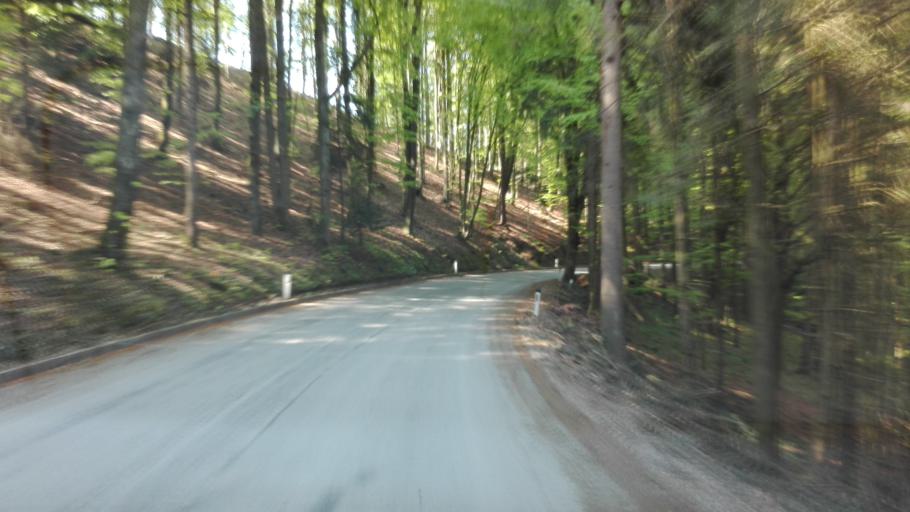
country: AT
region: Upper Austria
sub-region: Politischer Bezirk Rohrbach
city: Atzesberg
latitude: 48.4222
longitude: 13.9181
